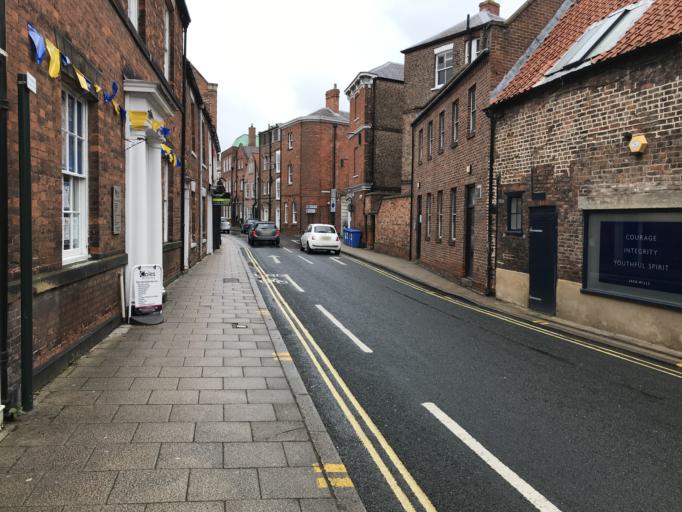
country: GB
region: England
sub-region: East Riding of Yorkshire
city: Beverley
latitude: 53.8426
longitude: -0.4331
